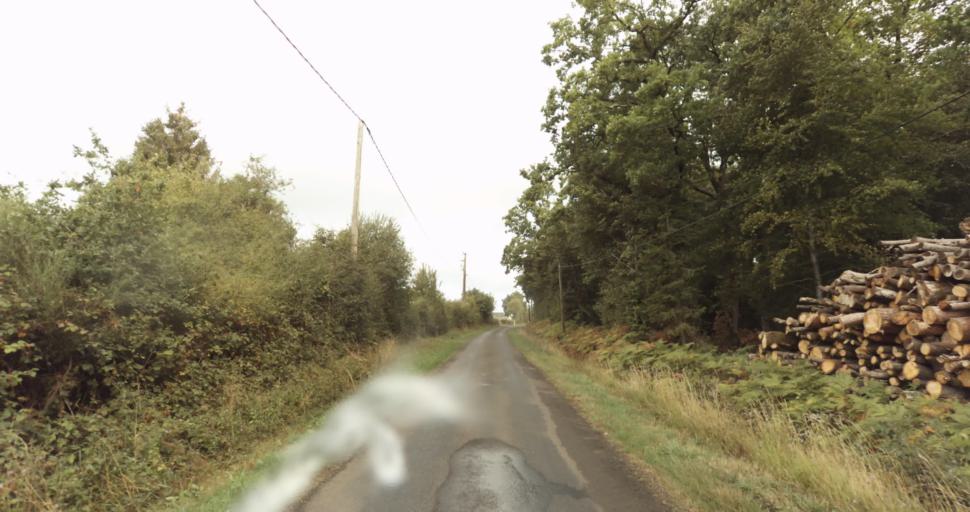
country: FR
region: Lower Normandy
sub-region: Departement de l'Orne
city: Gace
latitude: 48.8470
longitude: 0.3224
